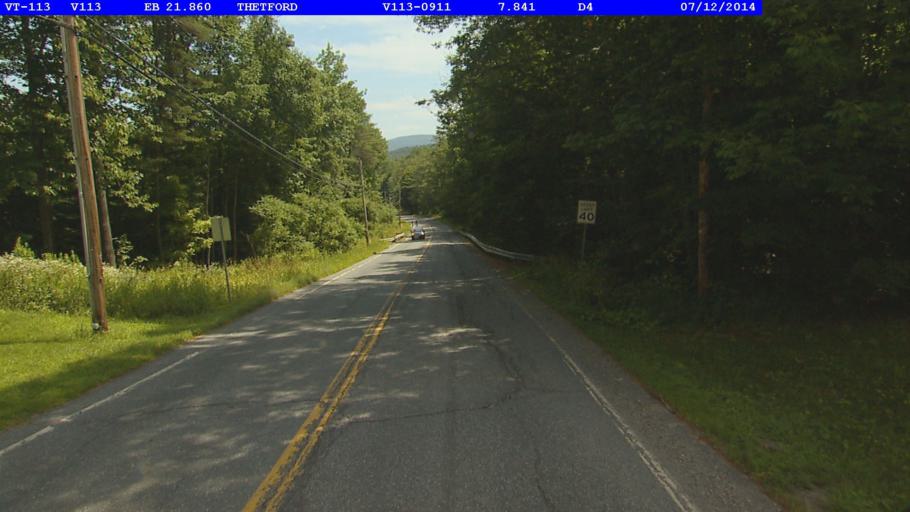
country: US
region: New Hampshire
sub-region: Grafton County
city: Lyme
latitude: 43.8129
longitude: -72.2008
